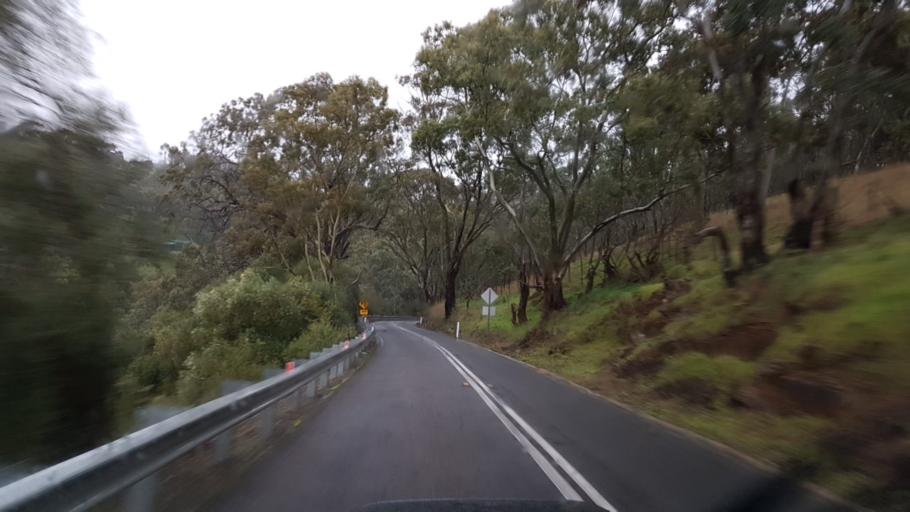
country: AU
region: South Australia
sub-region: Onkaparinga
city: Craigburn Farm
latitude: -35.0646
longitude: 138.6231
